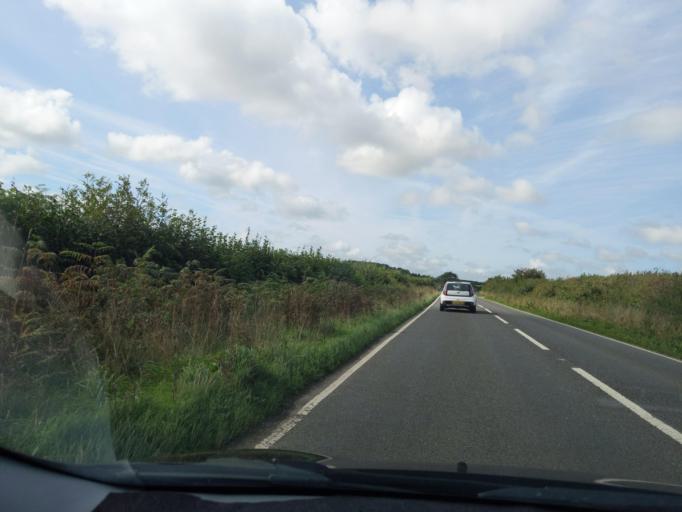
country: GB
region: England
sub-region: Cornwall
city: Trewen
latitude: 50.6267
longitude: -4.4528
